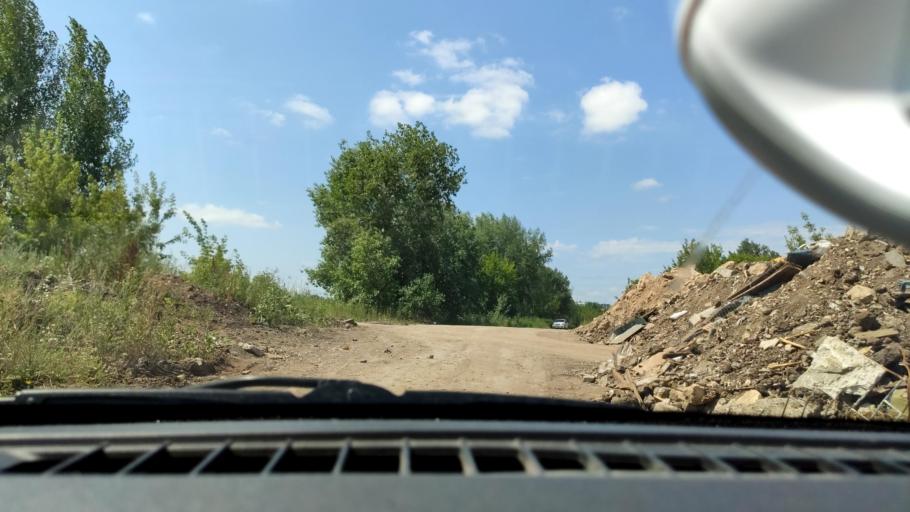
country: RU
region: Samara
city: Smyshlyayevka
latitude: 53.2049
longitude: 50.3202
